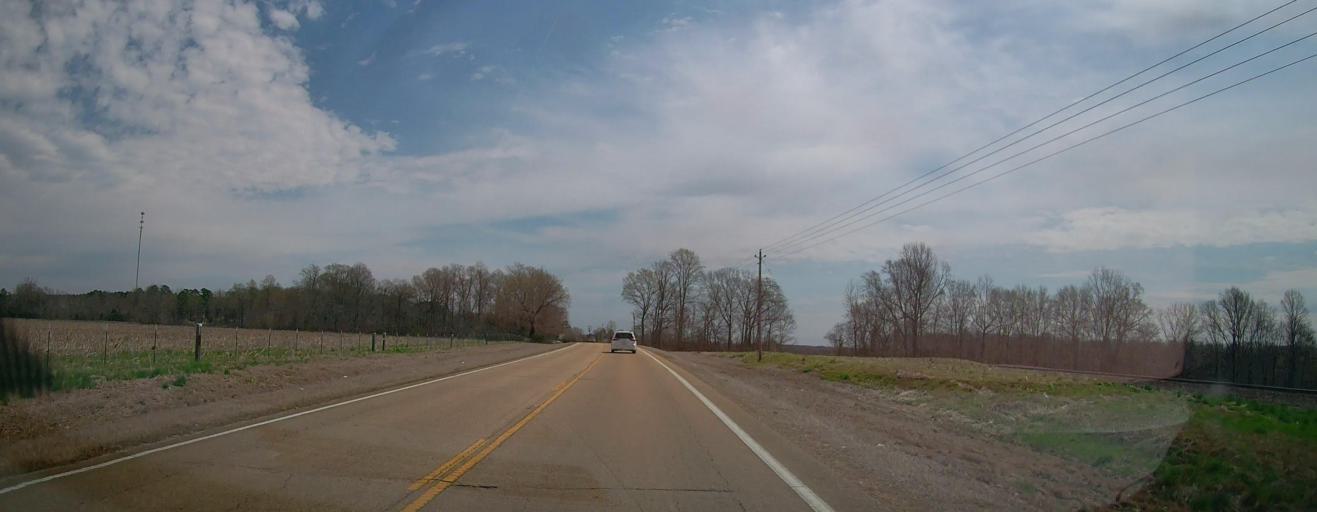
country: US
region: Mississippi
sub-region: Benton County
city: Ashland
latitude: 34.6192
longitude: -89.2235
